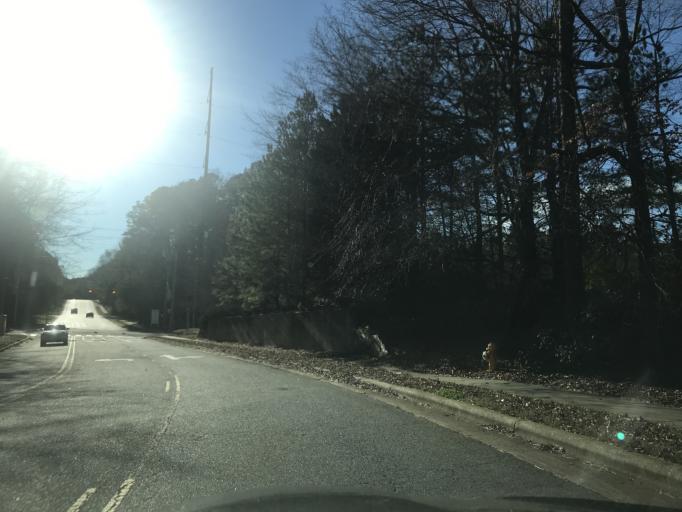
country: US
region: North Carolina
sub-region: Wake County
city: Cary
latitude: 35.8041
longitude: -78.7337
